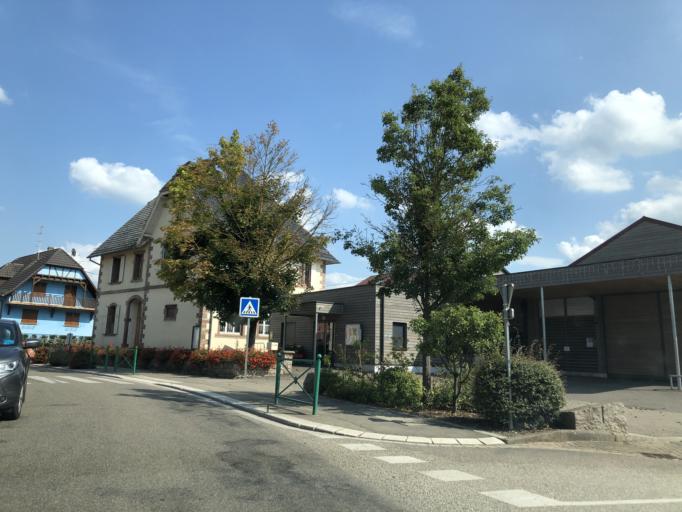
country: FR
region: Alsace
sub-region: Departement du Bas-Rhin
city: Matzenheim
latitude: 48.4282
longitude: 7.6229
